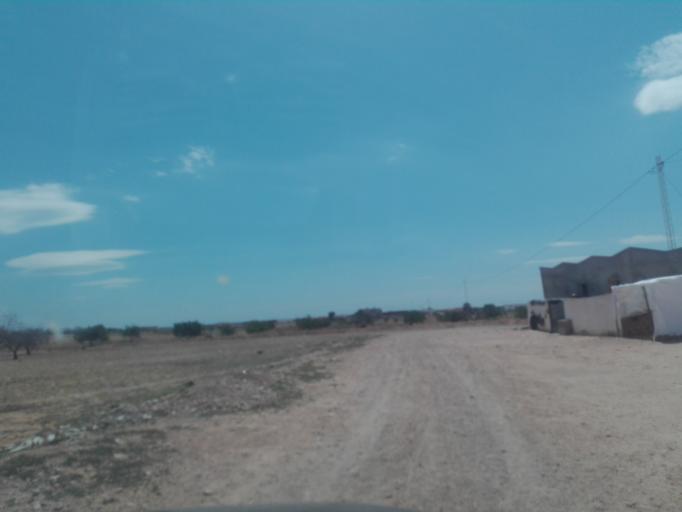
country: TN
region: Safaqis
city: Sfax
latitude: 34.6521
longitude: 10.5946
